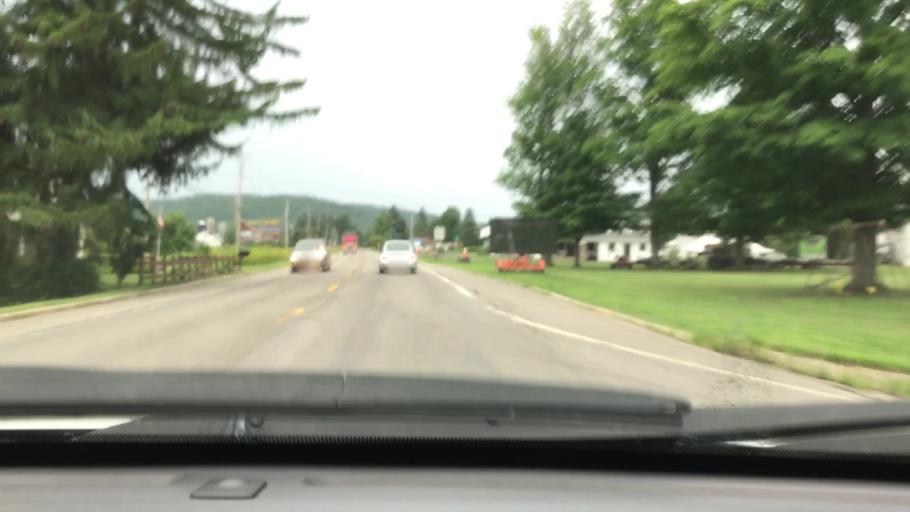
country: US
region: New York
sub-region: Cattaraugus County
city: Salamanca
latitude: 42.1947
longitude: -78.6582
